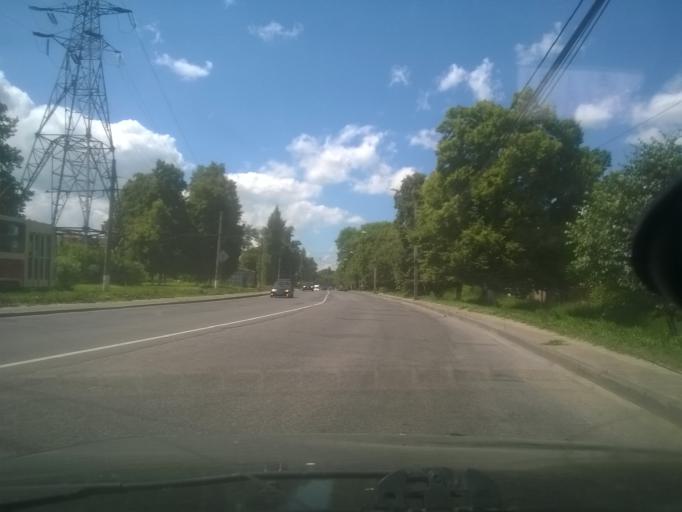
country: RU
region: Kursk
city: Voroshnevo
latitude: 51.6668
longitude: 36.1152
